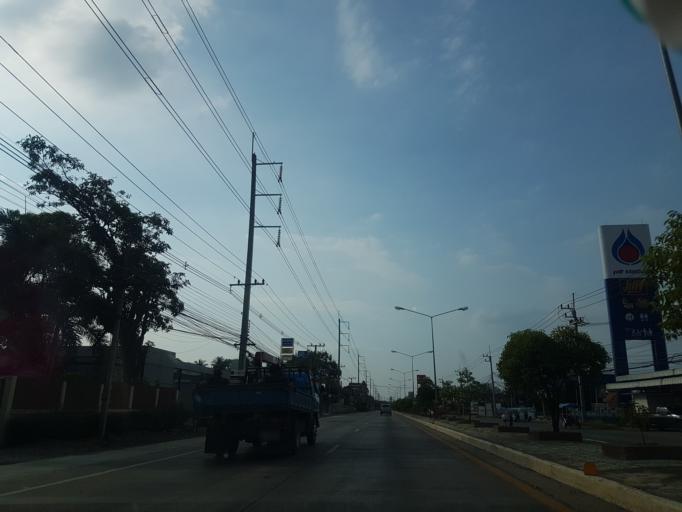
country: TH
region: Lop Buri
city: Lop Buri
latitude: 14.7674
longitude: 100.7096
